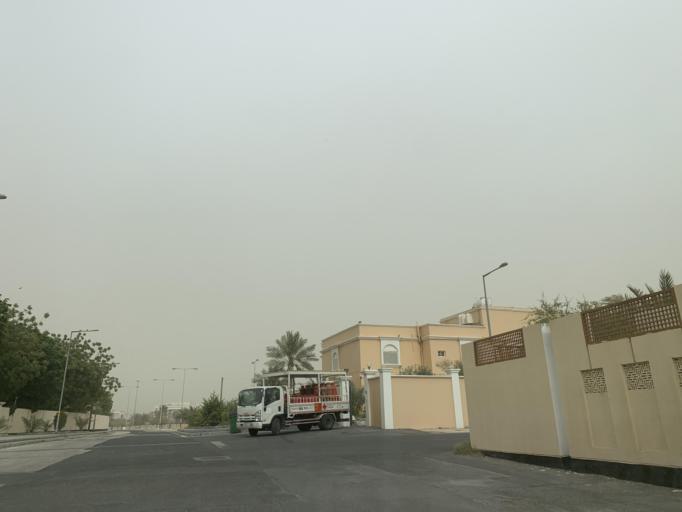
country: BH
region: Northern
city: Ar Rifa'
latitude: 26.1405
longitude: 50.5375
